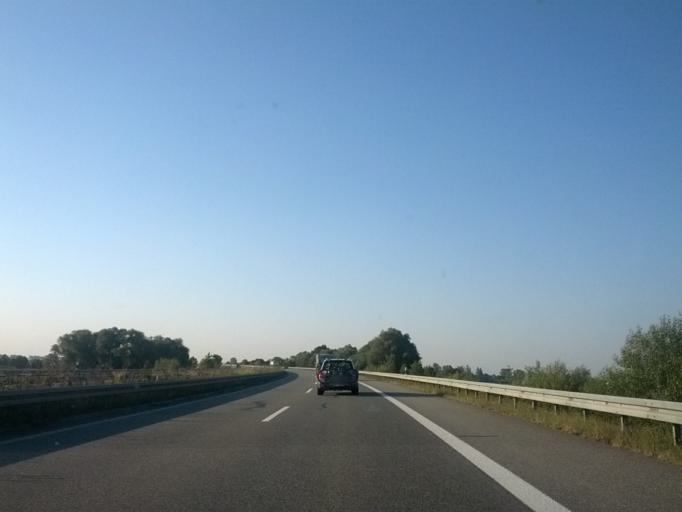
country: DE
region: Mecklenburg-Vorpommern
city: Wendorf
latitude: 54.2727
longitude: 13.0801
